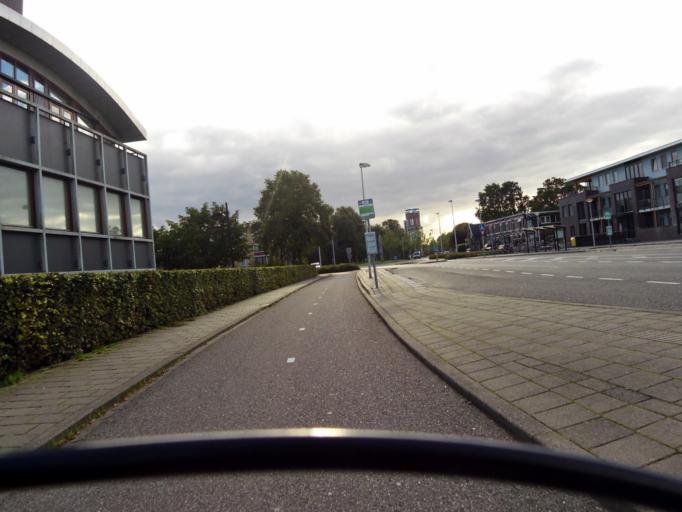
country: NL
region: South Holland
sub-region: Gemeente Leiderdorp
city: Leiderdorp
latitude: 52.1297
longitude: 4.5890
